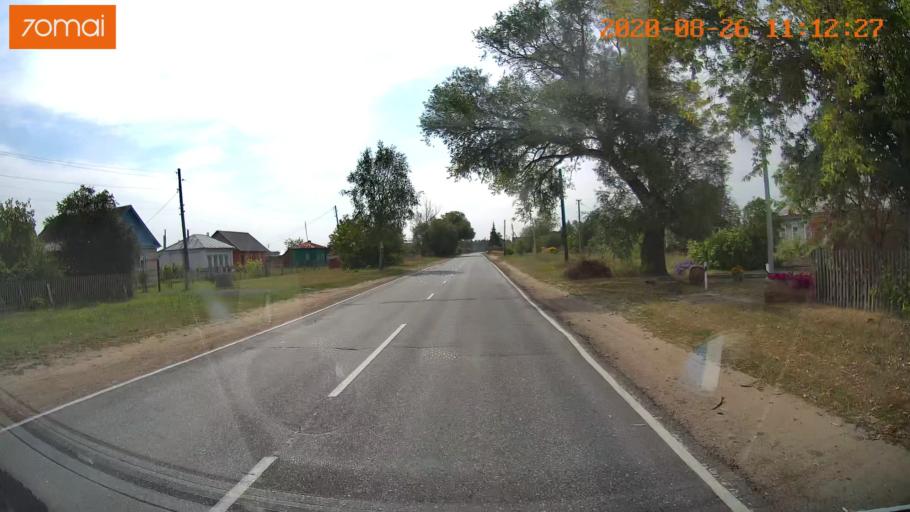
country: RU
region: Rjazan
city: Izhevskoye
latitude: 54.4704
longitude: 41.1252
